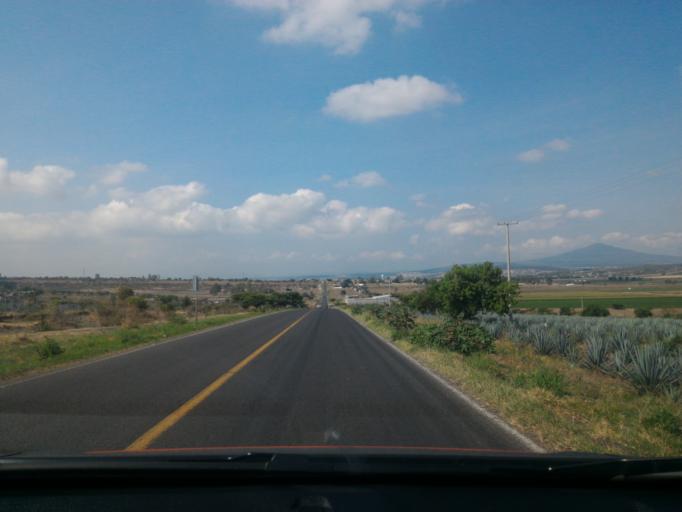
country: MX
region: Guanajuato
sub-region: Penjamo
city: Estacion la Piedad
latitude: 20.4234
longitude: -101.9929
